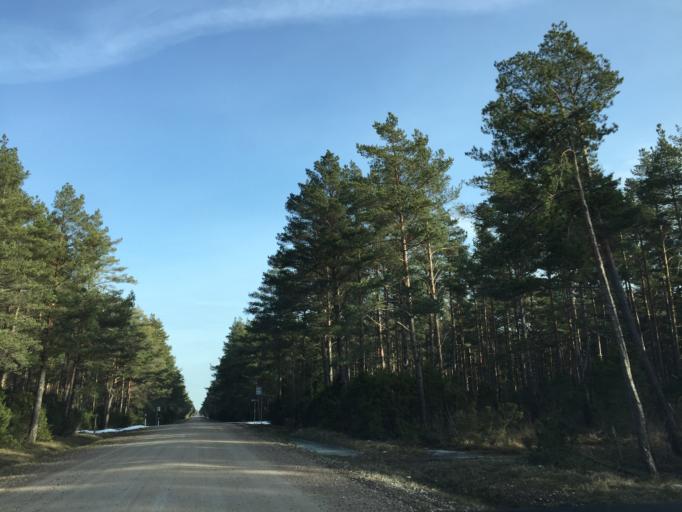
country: EE
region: Saare
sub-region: Kuressaare linn
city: Kuressaare
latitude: 58.2957
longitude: 21.9476
